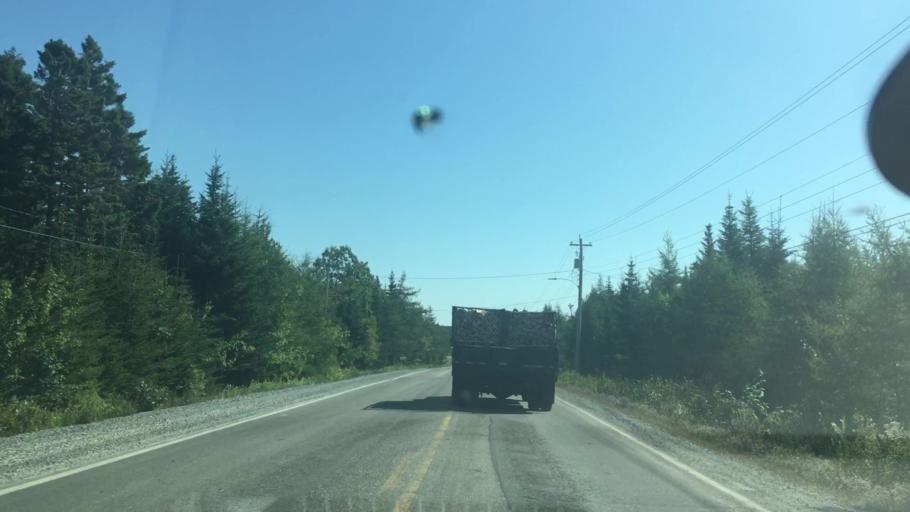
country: CA
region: Nova Scotia
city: New Glasgow
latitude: 44.9039
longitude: -62.4616
